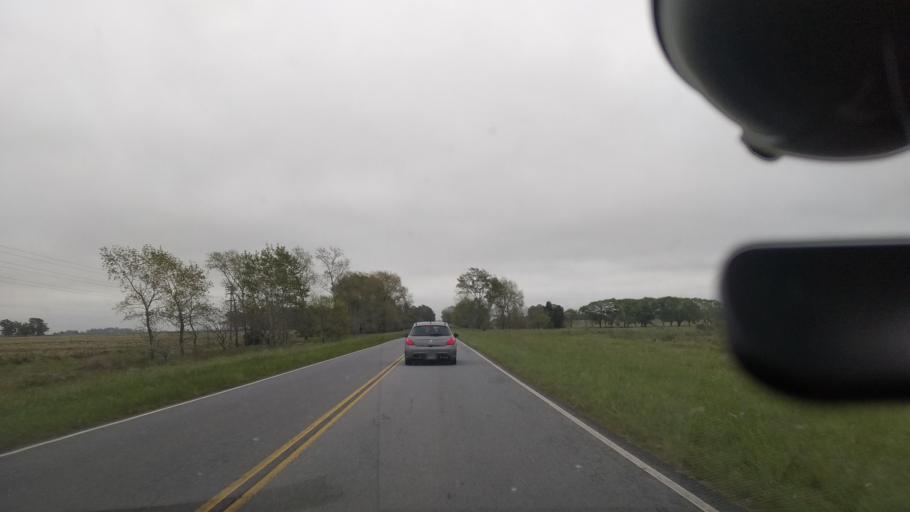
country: AR
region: Buenos Aires
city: Veronica
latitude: -35.3535
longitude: -57.4147
